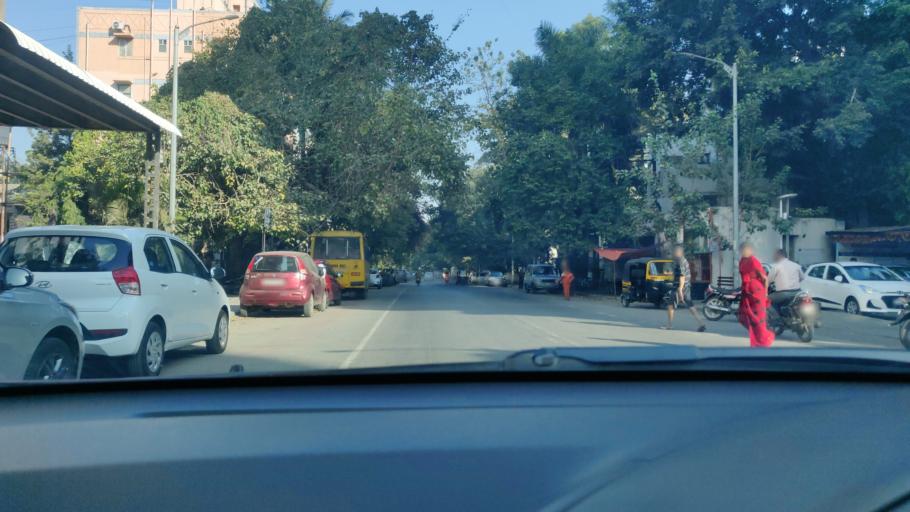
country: IN
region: Maharashtra
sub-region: Pune Division
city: Khadki
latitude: 18.5548
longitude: 73.8048
